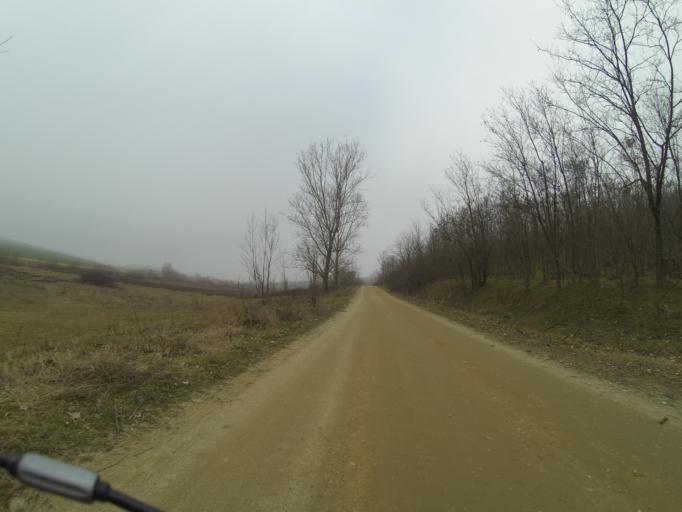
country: RO
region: Mehedinti
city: Padina Mica
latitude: 44.4831
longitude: 23.0340
